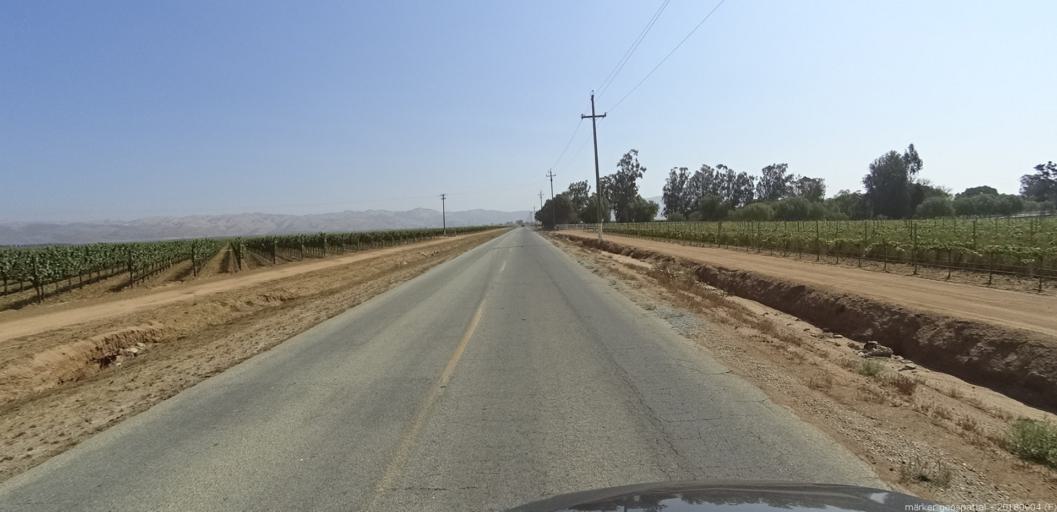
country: US
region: California
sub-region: Monterey County
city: Gonzales
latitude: 36.4990
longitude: -121.4051
